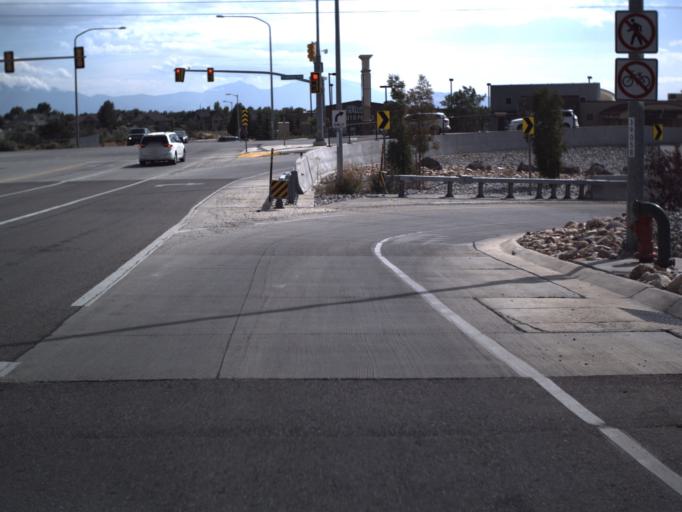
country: US
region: Utah
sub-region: Utah County
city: Alpine
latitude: 40.4327
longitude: -111.8220
